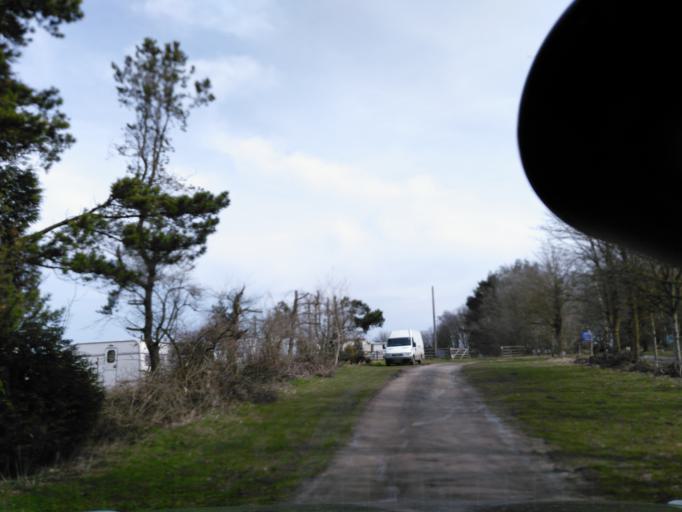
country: GB
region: England
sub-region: North Yorkshire
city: Angram Grange
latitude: 54.2294
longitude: -1.2085
